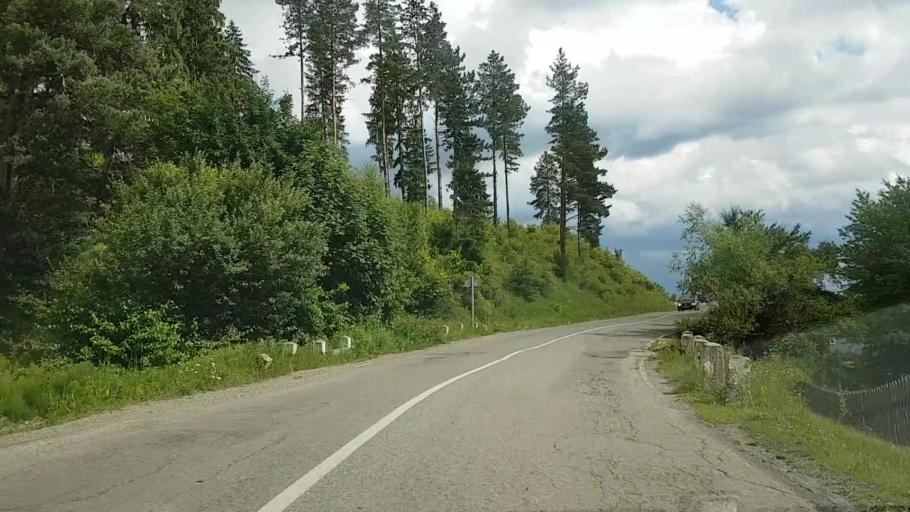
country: RO
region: Neamt
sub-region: Comuna Hangu
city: Hangu
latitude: 47.0088
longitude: 26.0897
